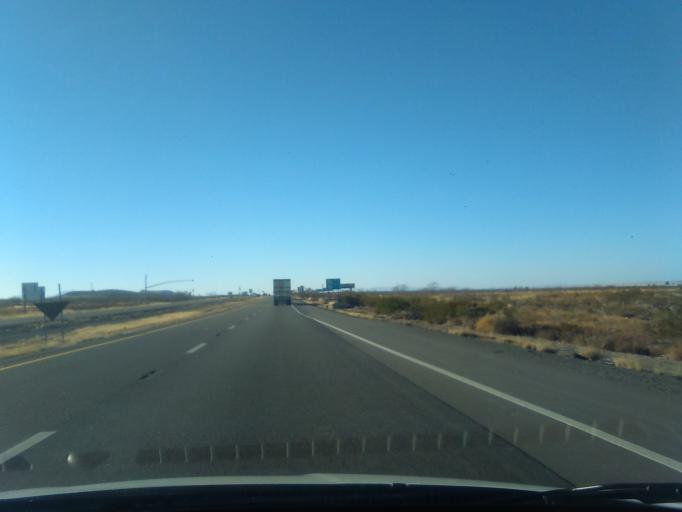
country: US
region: New Mexico
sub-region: Hidalgo County
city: Lordsburg
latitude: 32.3441
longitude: -108.7169
